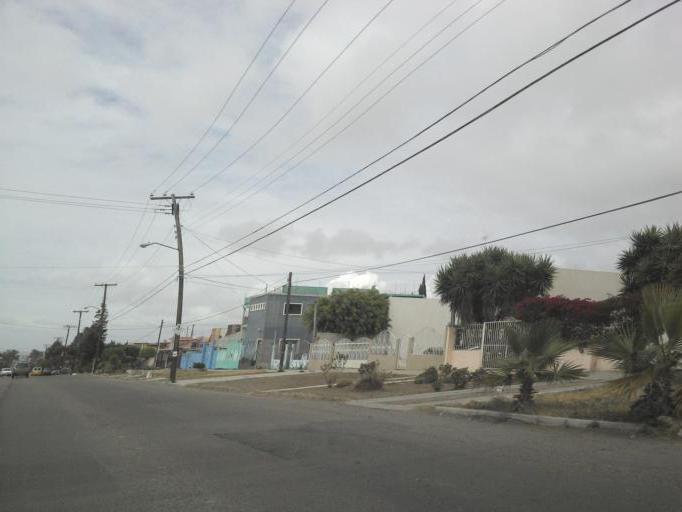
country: MX
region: Baja California
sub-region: Tijuana
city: La Esperanza [Granjas Familiares]
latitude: 32.5158
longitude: -117.1124
